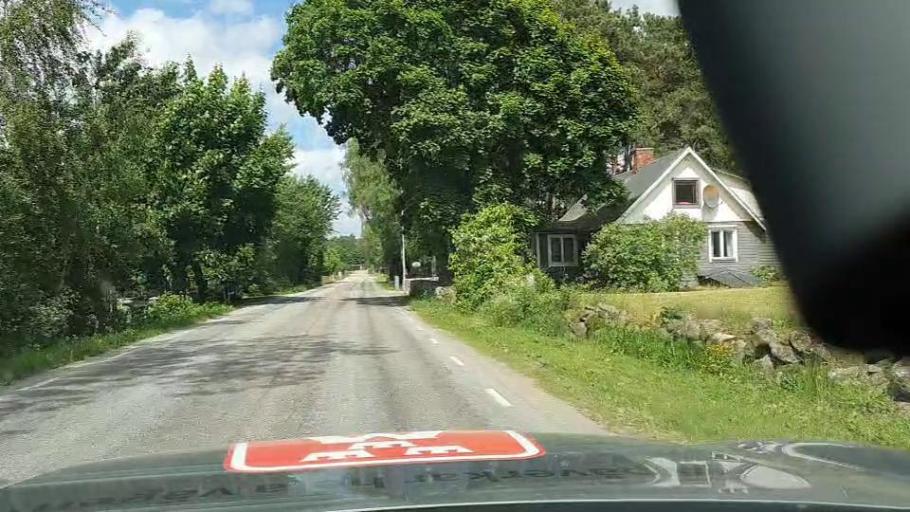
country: SE
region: Blekinge
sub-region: Karlshamns Kommun
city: Morrum
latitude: 56.1073
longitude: 14.6848
